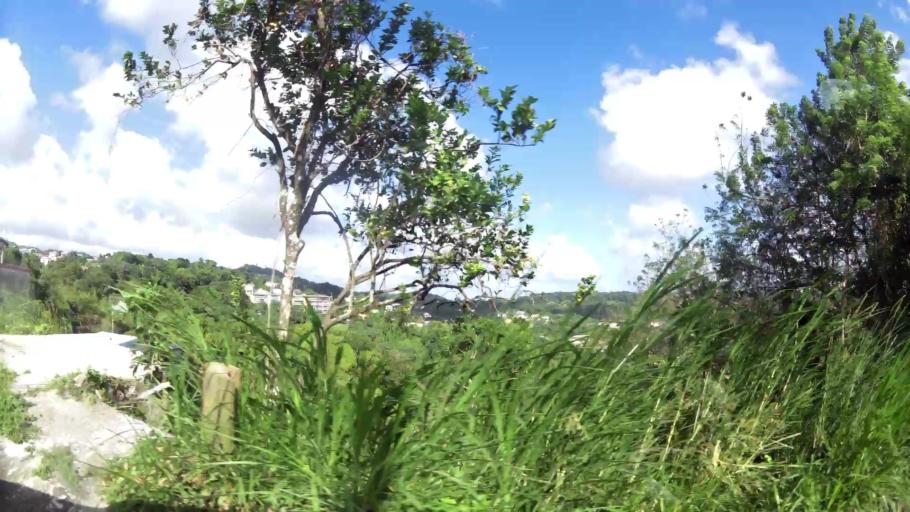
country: MQ
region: Martinique
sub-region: Martinique
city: Fort-de-France
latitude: 14.6408
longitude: -61.0749
